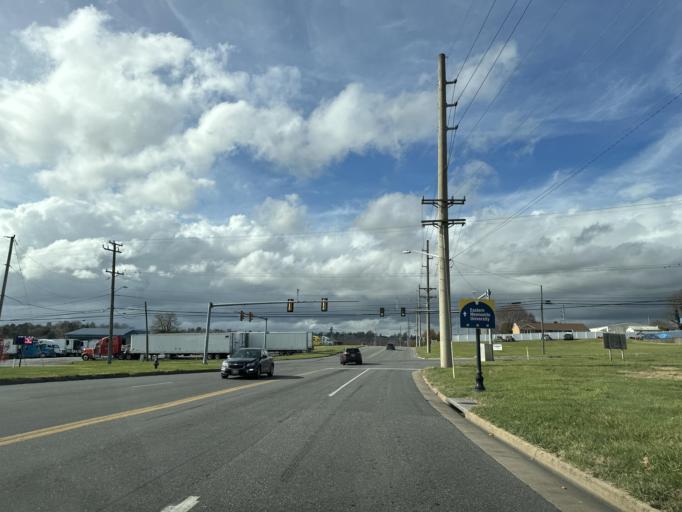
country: US
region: Virginia
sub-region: City of Harrisonburg
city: Harrisonburg
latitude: 38.4668
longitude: -78.8620
